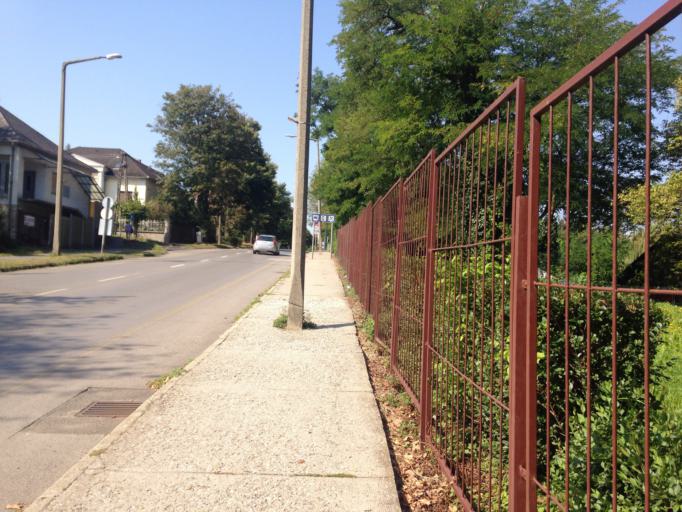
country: HU
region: Somogy
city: Kaposvar
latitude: 46.3681
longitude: 17.7944
